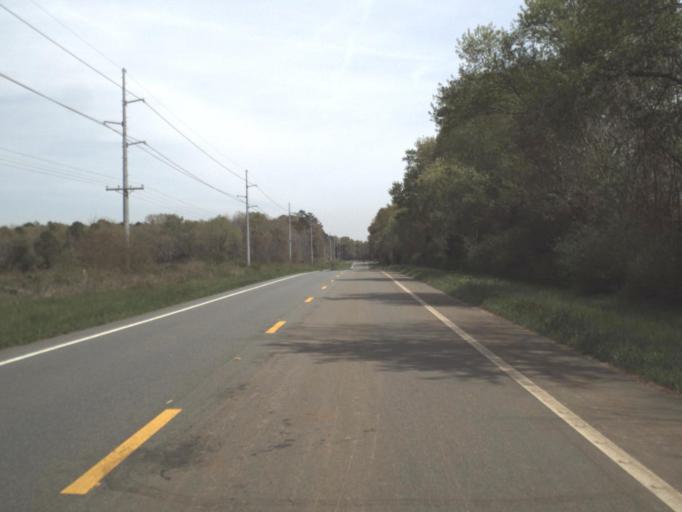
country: US
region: Alabama
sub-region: Houston County
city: Cottonwood
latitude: 30.9357
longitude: -85.3113
